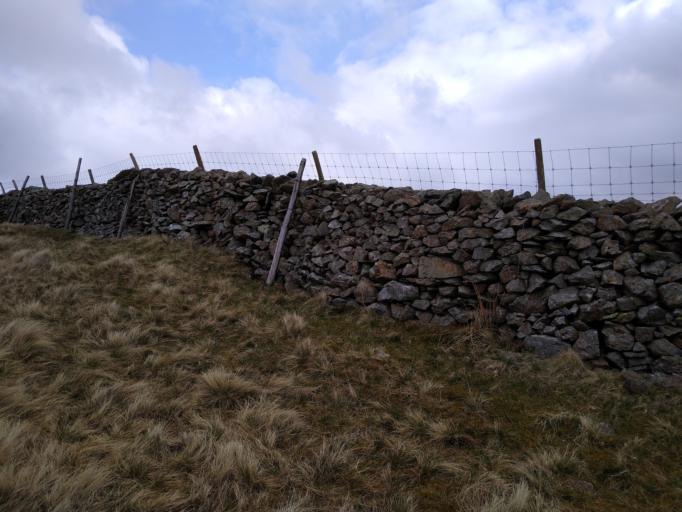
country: GB
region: England
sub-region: Cumbria
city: Windermere
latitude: 54.4394
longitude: -2.8678
